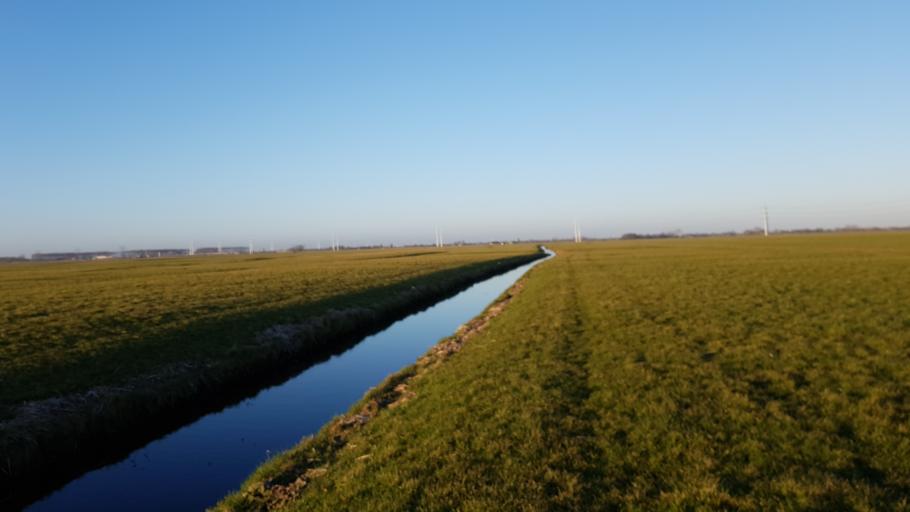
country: NL
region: South Holland
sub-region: Gemeente Leiderdorp
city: Leiderdorp
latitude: 52.1372
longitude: 4.5602
